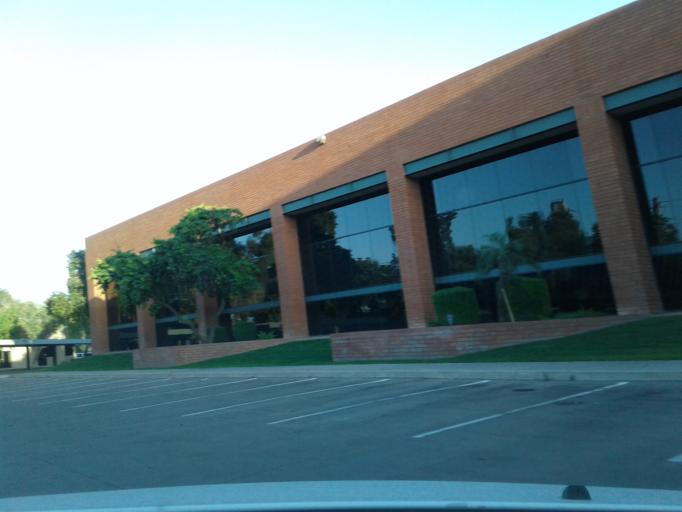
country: US
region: Arizona
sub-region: Maricopa County
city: Glendale
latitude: 33.5699
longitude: -112.1114
